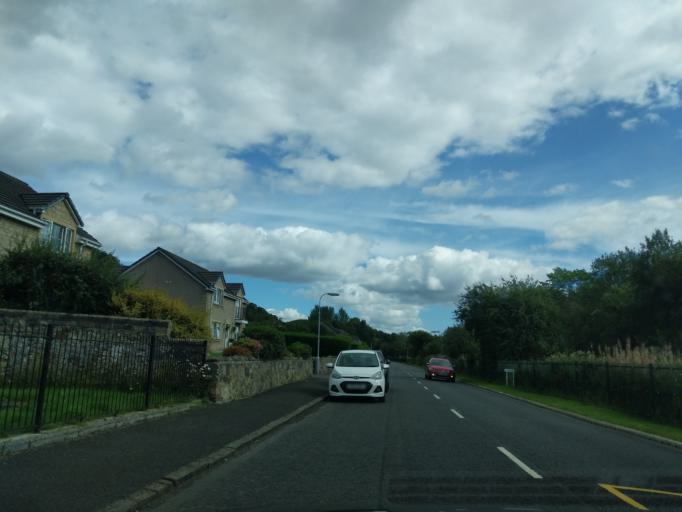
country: GB
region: Scotland
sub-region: Fife
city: High Valleyfield
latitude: 56.0589
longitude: -3.6034
